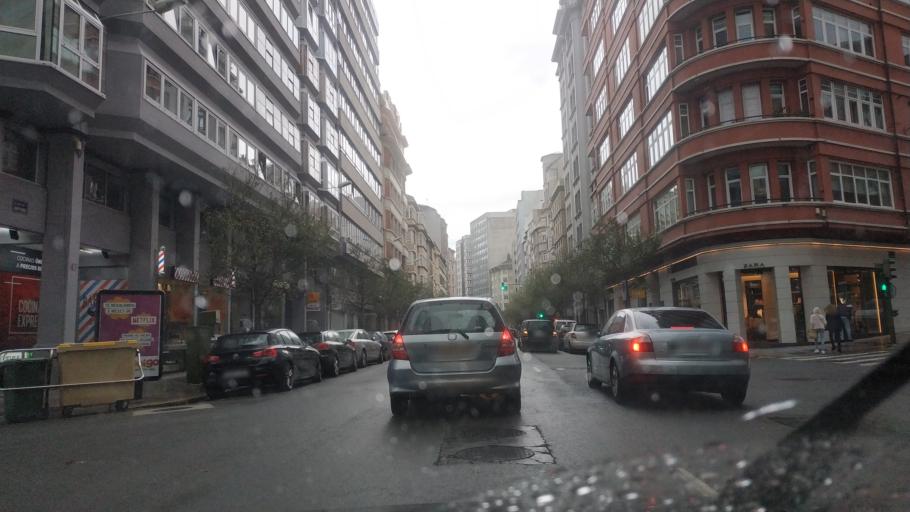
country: ES
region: Galicia
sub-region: Provincia da Coruna
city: A Coruna
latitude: 43.3638
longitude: -8.4081
